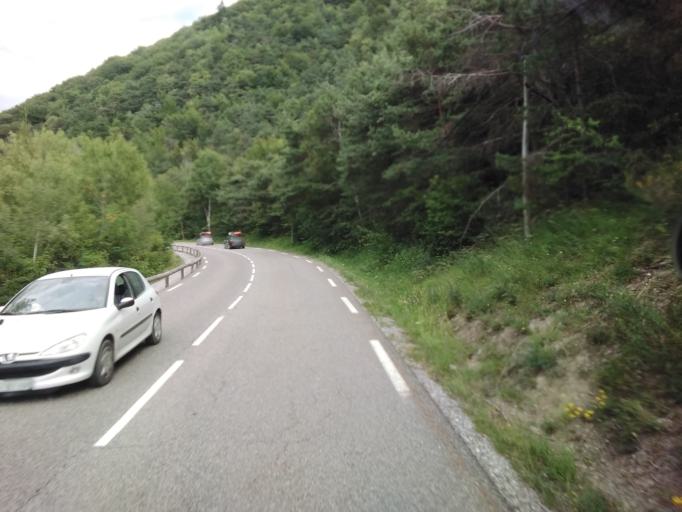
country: FR
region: Provence-Alpes-Cote d'Azur
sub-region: Departement des Hautes-Alpes
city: Chorges
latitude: 44.5191
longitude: 6.3883
